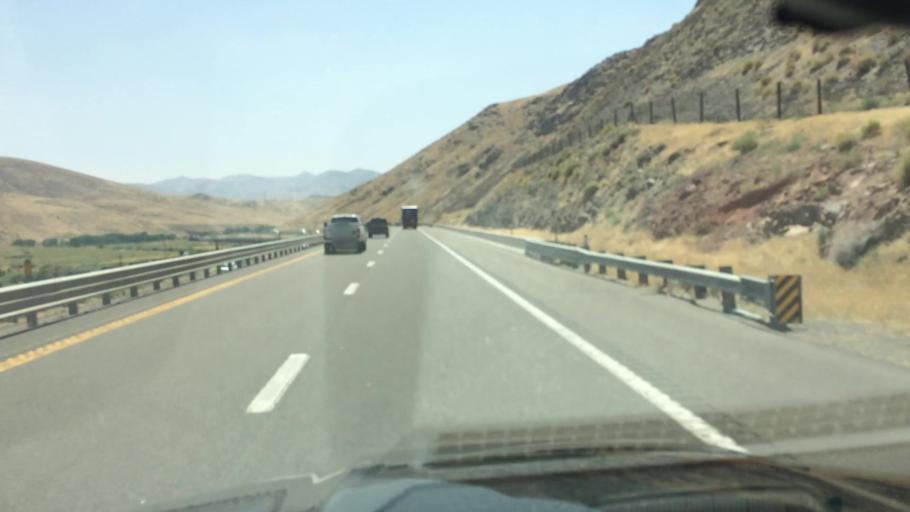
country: US
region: Nevada
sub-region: Lyon County
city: Fernley
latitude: 39.5814
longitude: -119.4704
